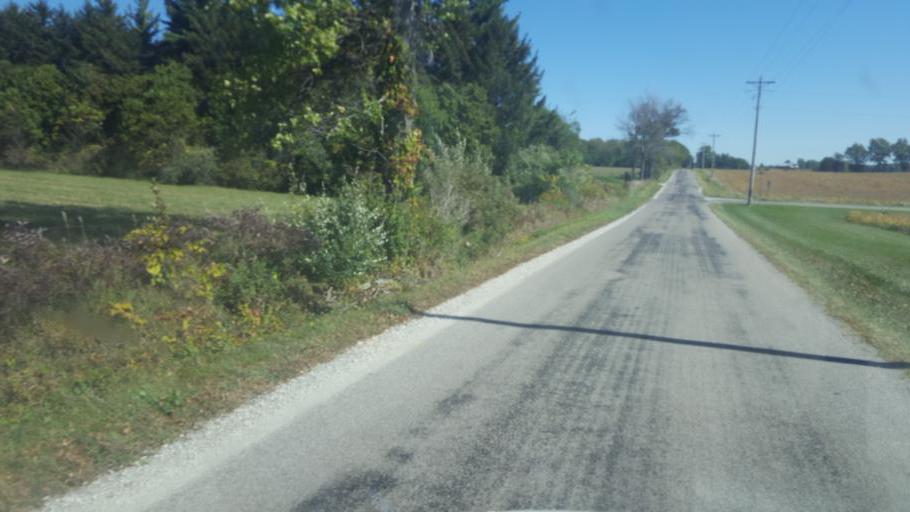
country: US
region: Ohio
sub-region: Huron County
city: Willard
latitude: 40.9457
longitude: -82.8125
